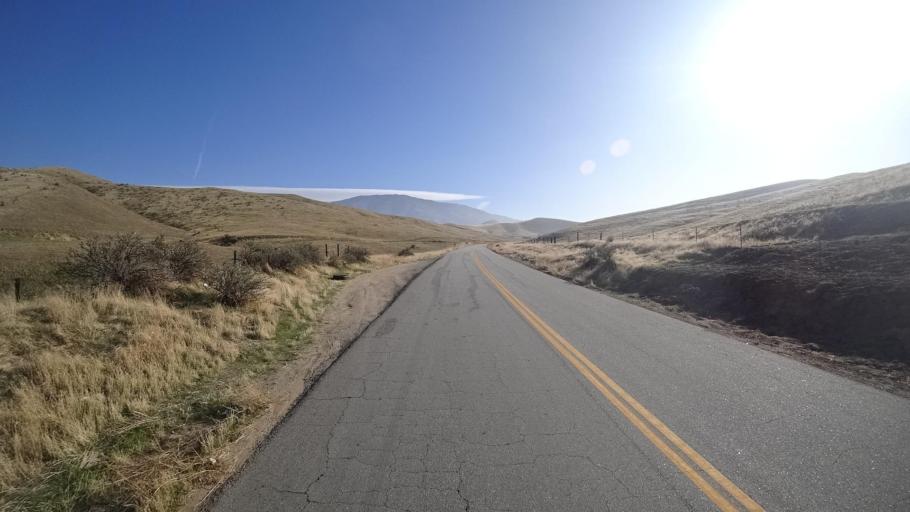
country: US
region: California
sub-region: Kern County
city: Bear Valley Springs
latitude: 35.2901
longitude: -118.6954
